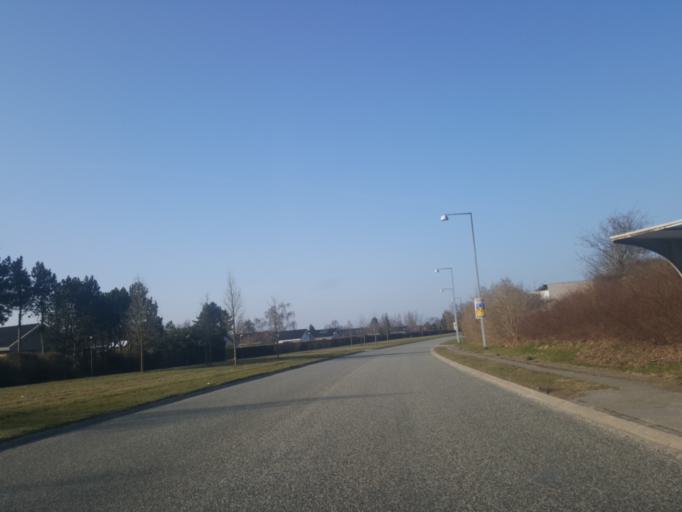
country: DK
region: Capital Region
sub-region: Allerod Kommune
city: Lillerod
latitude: 55.8683
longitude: 12.3283
